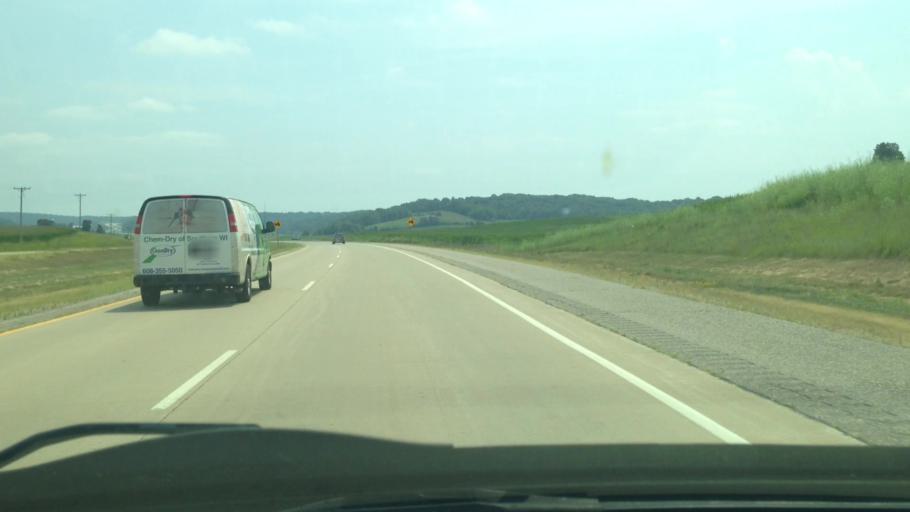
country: US
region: Wisconsin
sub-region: Sauk County
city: Sauk City
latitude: 43.2241
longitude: -89.6695
